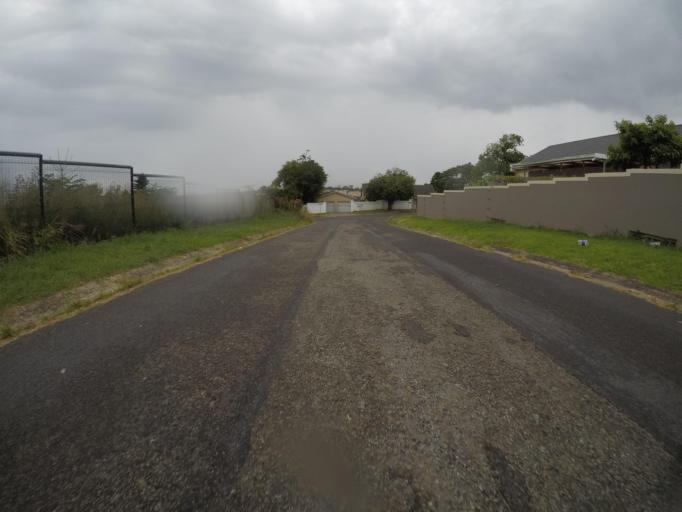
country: ZA
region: Eastern Cape
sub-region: Buffalo City Metropolitan Municipality
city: East London
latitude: -32.9912
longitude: 27.8475
